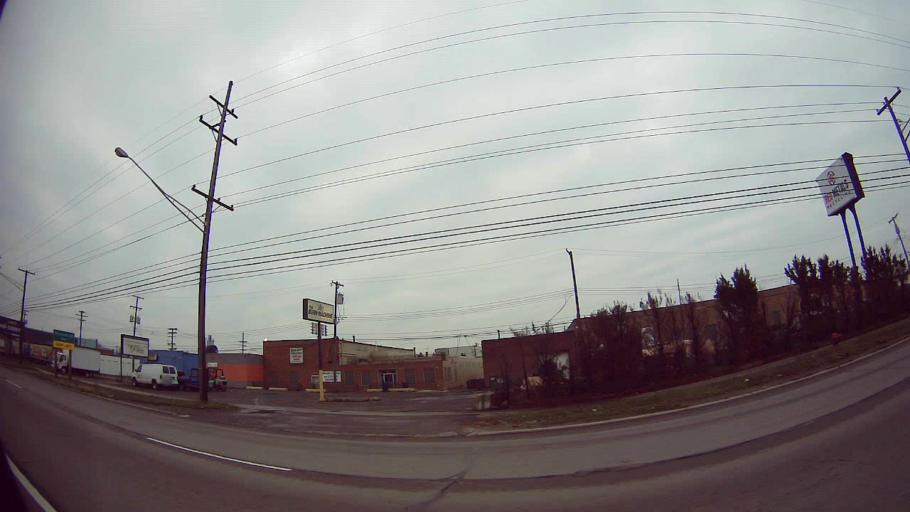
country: US
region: Michigan
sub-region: Wayne County
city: Redford
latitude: 42.3744
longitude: -83.2757
